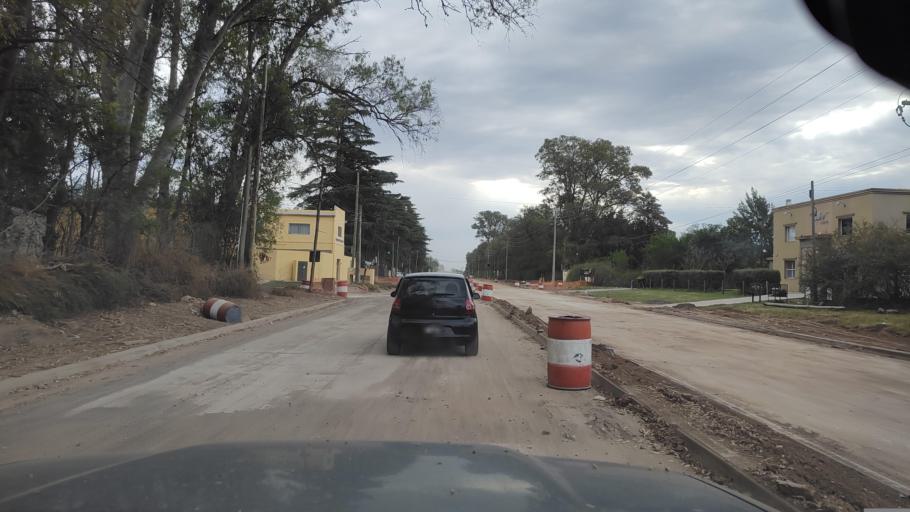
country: AR
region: Buenos Aires
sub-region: Partido de Lujan
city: Lujan
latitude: -34.5526
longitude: -59.0922
